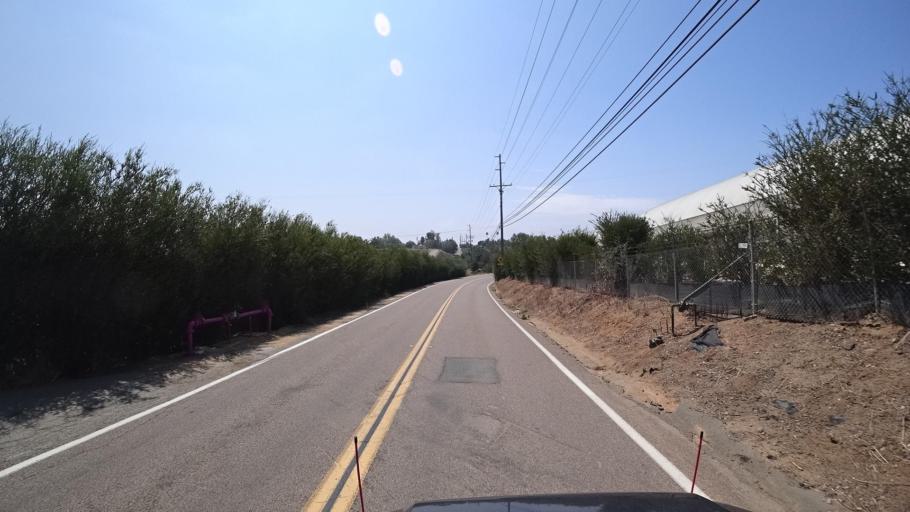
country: US
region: California
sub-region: San Diego County
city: Fallbrook
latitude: 33.3504
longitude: -117.2304
